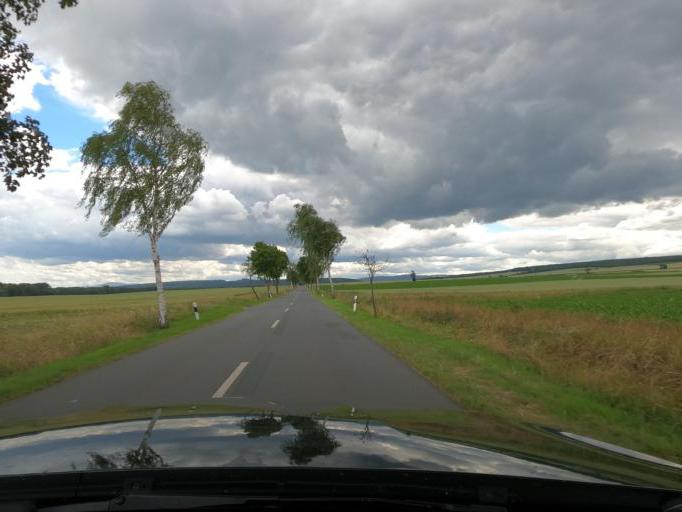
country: DE
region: Lower Saxony
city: Heere
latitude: 52.0601
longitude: 10.2527
